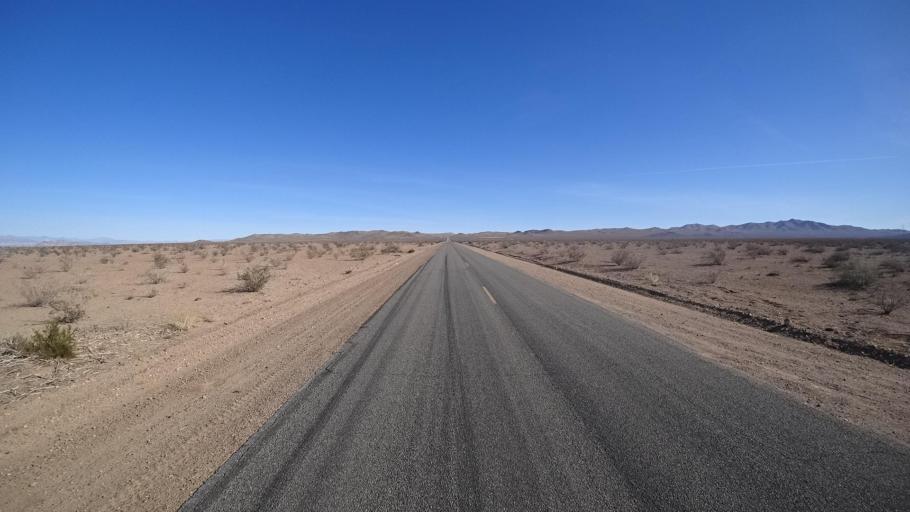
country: US
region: California
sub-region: Kern County
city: China Lake Acres
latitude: 35.5592
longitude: -117.7602
